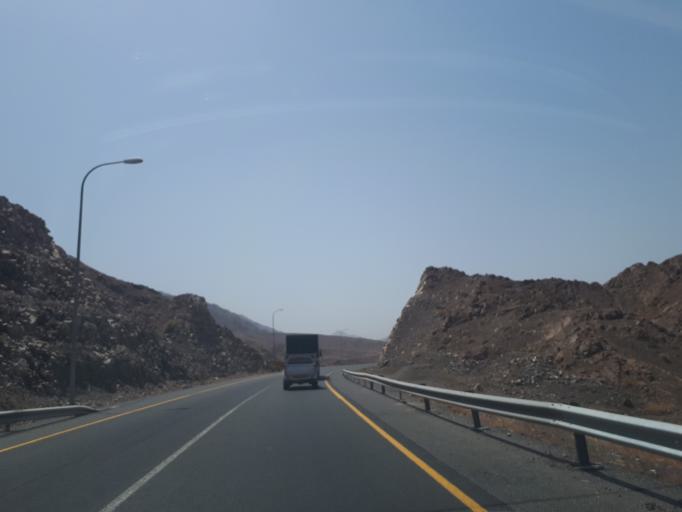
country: OM
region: Muhafazat ad Dakhiliyah
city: Sufalat Sama'il
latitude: 23.2089
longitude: 58.0799
